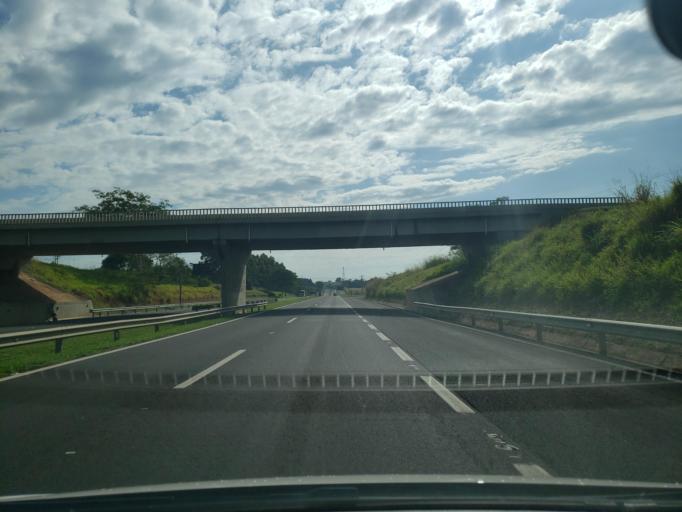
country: BR
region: Sao Paulo
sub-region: Lins
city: Lins
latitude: -21.6815
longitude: -49.7679
